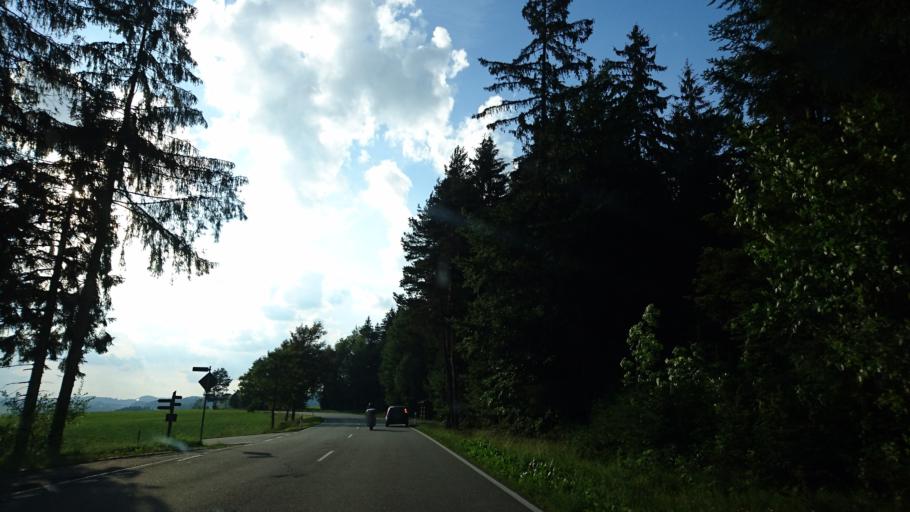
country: DE
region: Bavaria
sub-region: Lower Bavaria
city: Grafenau
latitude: 48.8712
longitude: 13.4296
